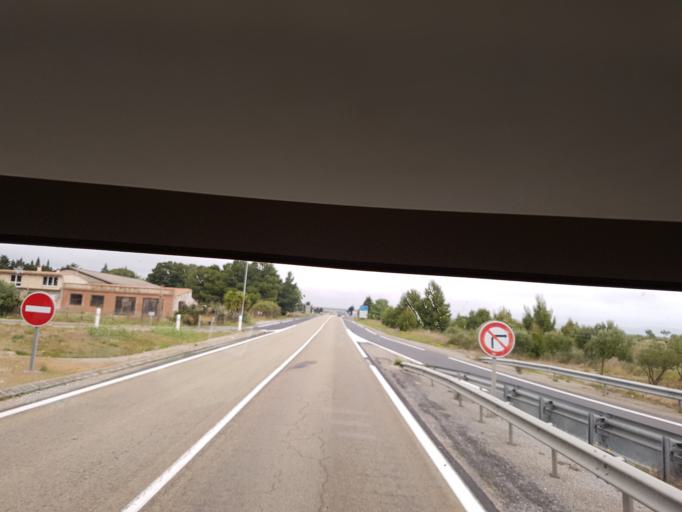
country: FR
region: Languedoc-Roussillon
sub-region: Departement de l'Aude
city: Leucate
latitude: 42.9318
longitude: 2.9926
